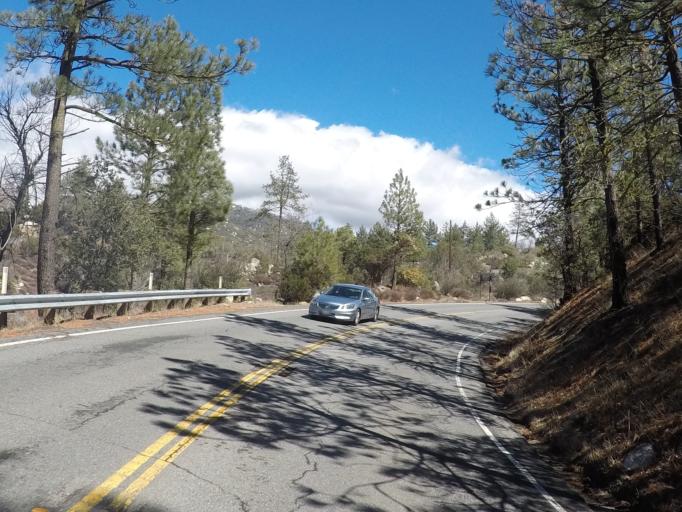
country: US
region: California
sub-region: Riverside County
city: Idyllwild
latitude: 33.7056
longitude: -116.7306
